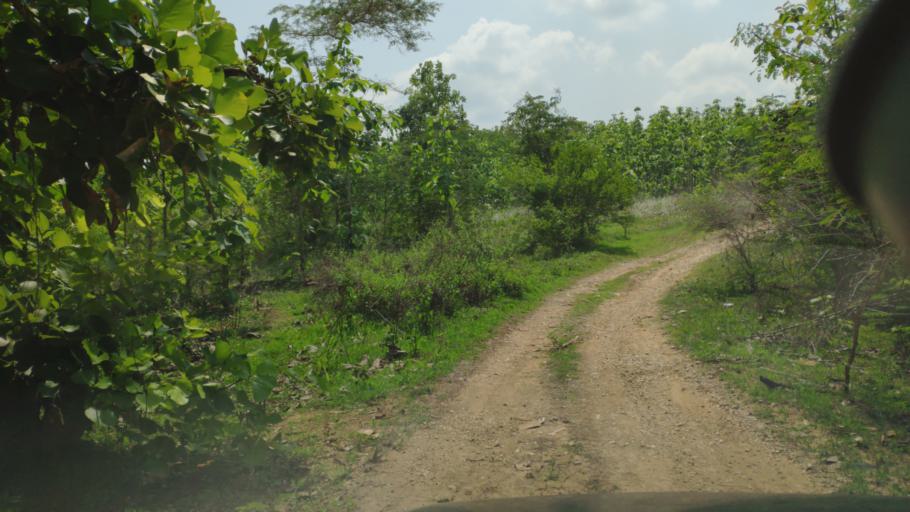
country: ID
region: Central Java
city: Gaplokan
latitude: -6.9116
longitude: 111.2682
